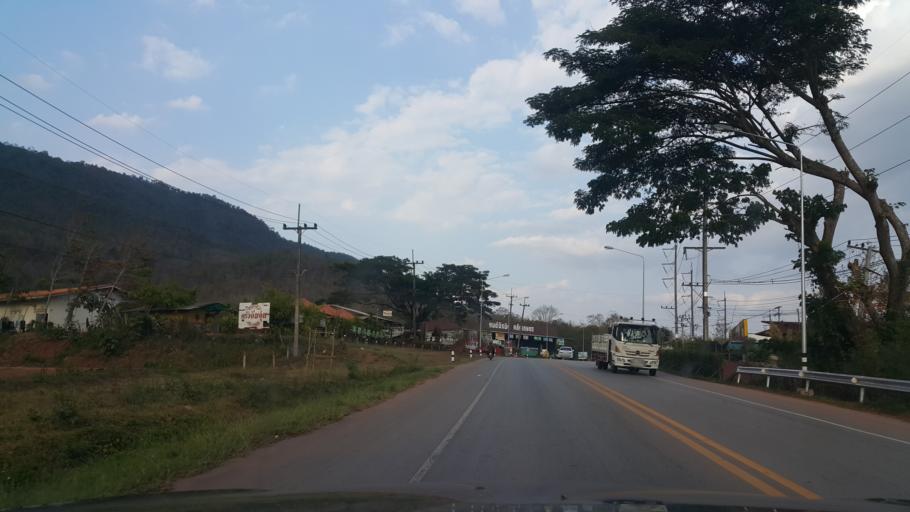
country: TH
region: Loei
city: Dan Sai
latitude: 17.2868
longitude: 101.1834
